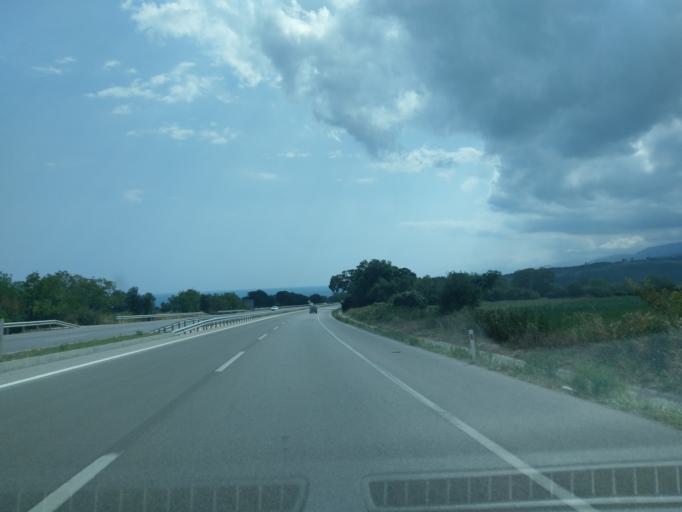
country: TR
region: Sinop
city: Kabali
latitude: 41.8463
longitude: 35.1347
